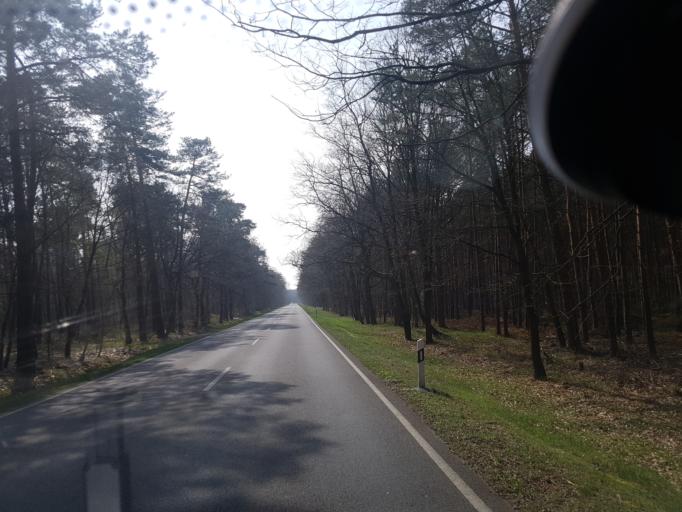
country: DE
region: Brandenburg
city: Luebben
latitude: 51.9677
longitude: 13.9488
